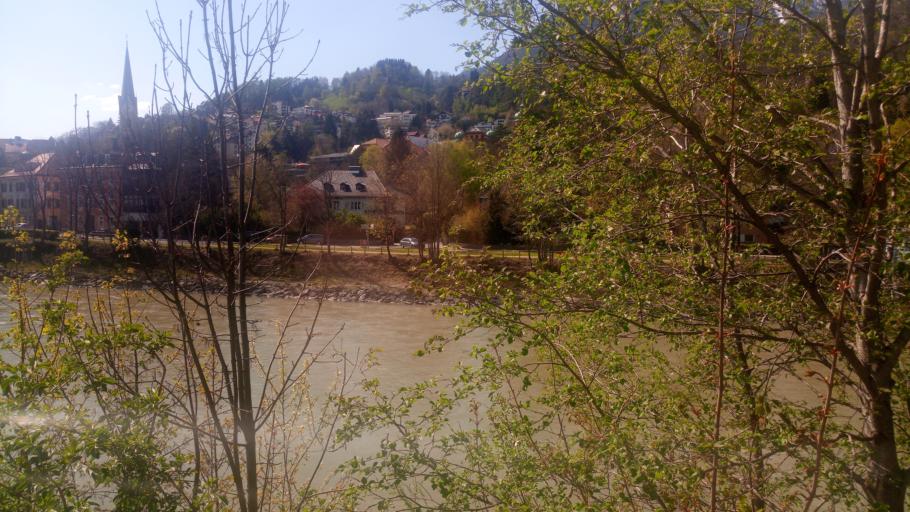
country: AT
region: Tyrol
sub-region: Innsbruck Stadt
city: Innsbruck
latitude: 47.2771
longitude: 11.3975
